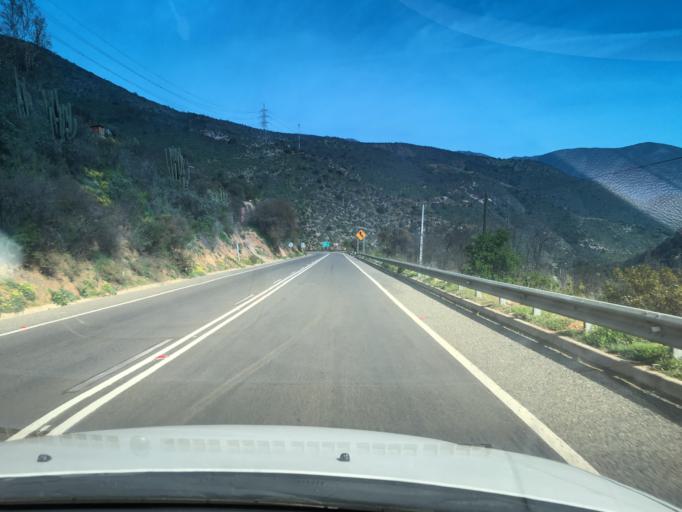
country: CL
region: Valparaiso
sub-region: Provincia de Marga Marga
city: Limache
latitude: -33.0628
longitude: -71.0625
